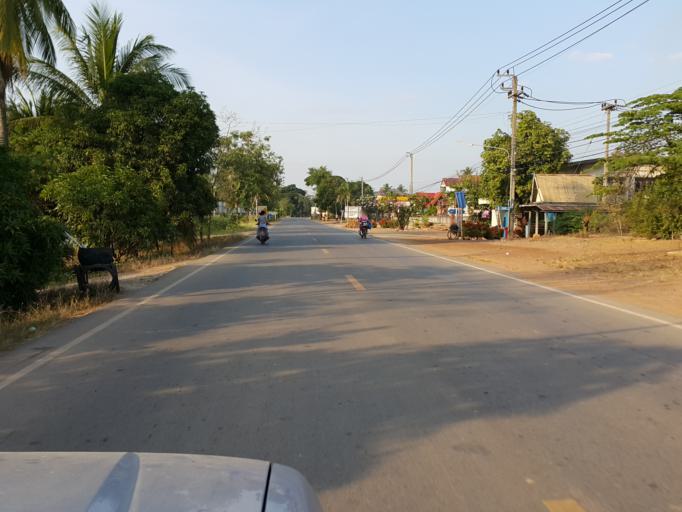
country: TH
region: Sukhothai
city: Sawankhalok
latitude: 17.4153
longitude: 99.7987
